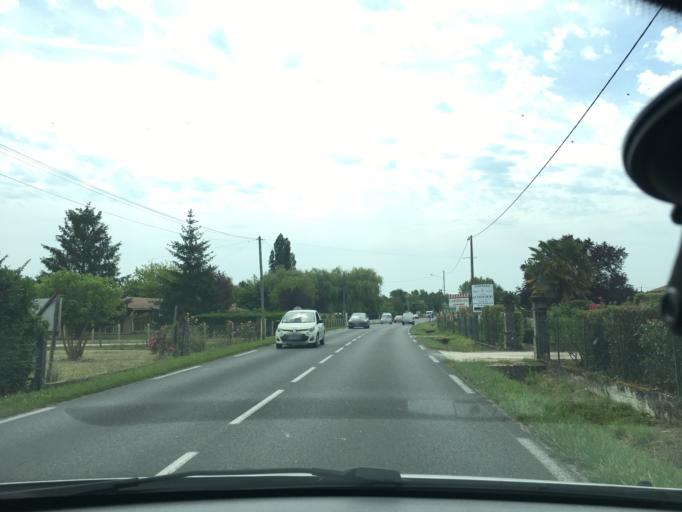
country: FR
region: Aquitaine
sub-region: Departement de la Gironde
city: Gaillan-en-Medoc
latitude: 45.3185
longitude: -0.9528
